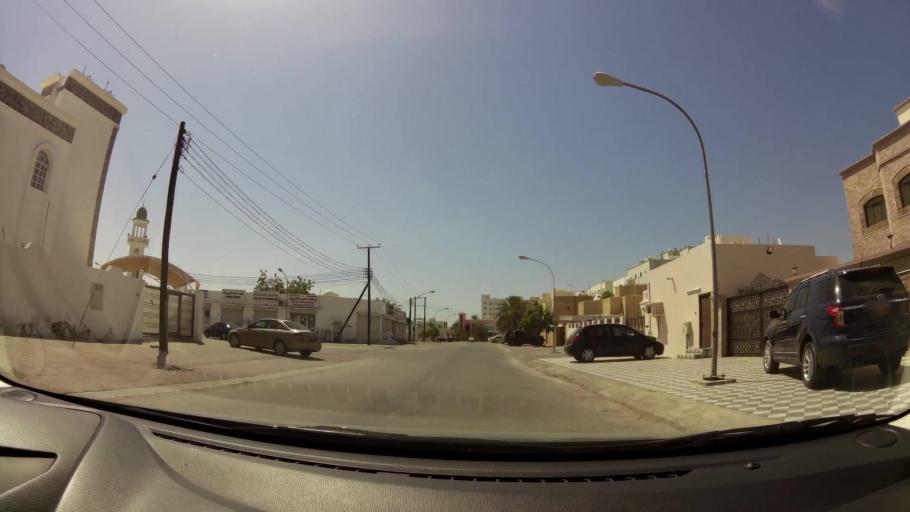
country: OM
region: Muhafazat Masqat
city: As Sib al Jadidah
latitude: 23.6240
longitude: 58.2193
